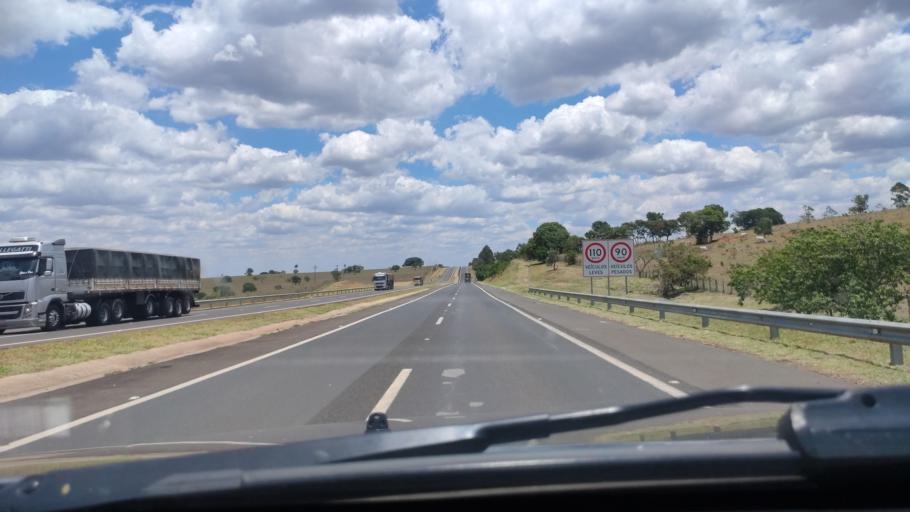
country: BR
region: Sao Paulo
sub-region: Duartina
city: Duartina
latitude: -22.4975
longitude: -49.2676
